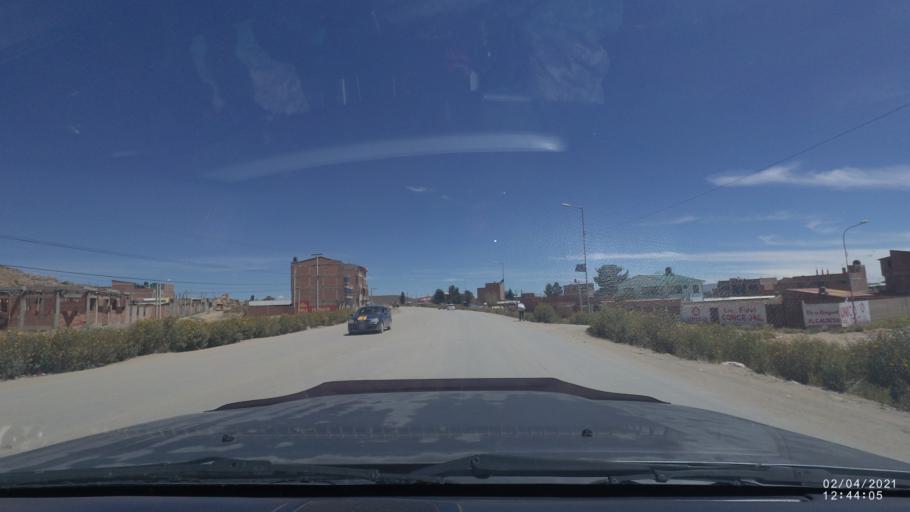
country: BO
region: Oruro
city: Oruro
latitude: -17.9277
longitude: -67.1258
